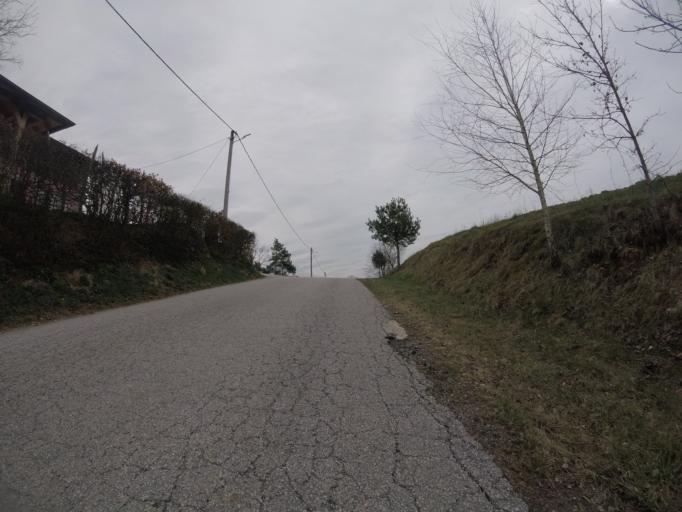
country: HR
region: Zagrebacka
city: Lukavec
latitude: 45.5431
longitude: 15.9867
